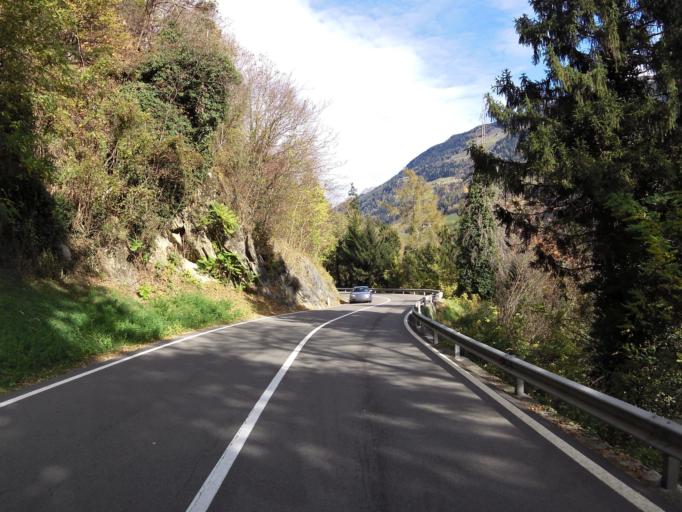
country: IT
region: Trentino-Alto Adige
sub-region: Bolzano
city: Rifiano
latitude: 46.7234
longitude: 11.1932
